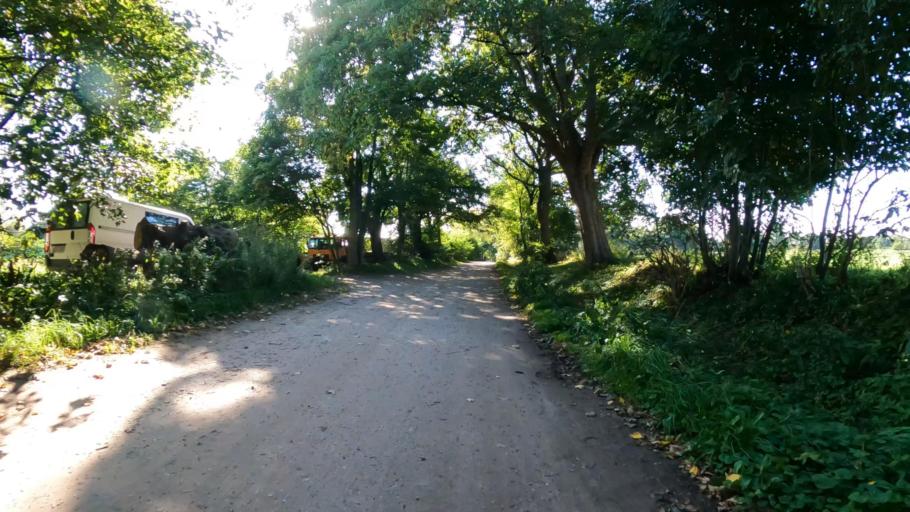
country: DE
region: Schleswig-Holstein
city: Ahrensburg
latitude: 53.6642
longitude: 10.2009
